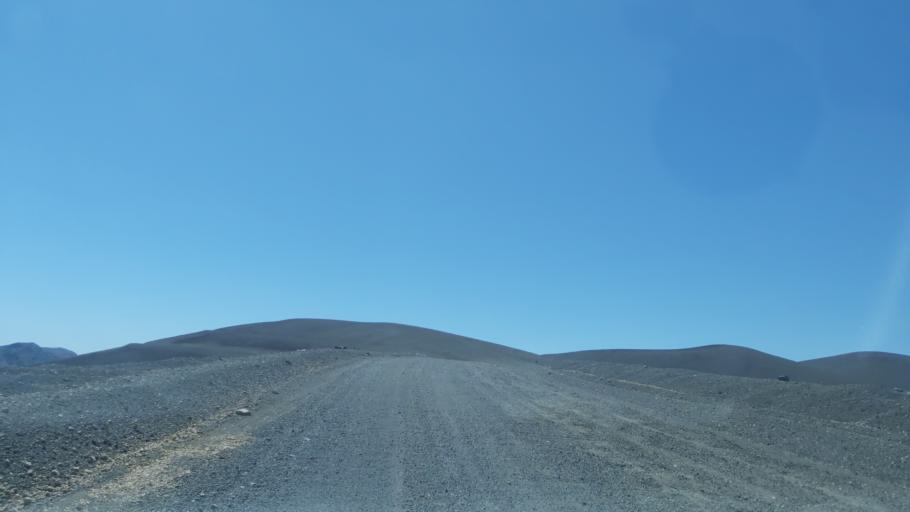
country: CL
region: Araucania
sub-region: Provincia de Cautin
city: Vilcun
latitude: -38.3748
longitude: -71.5398
